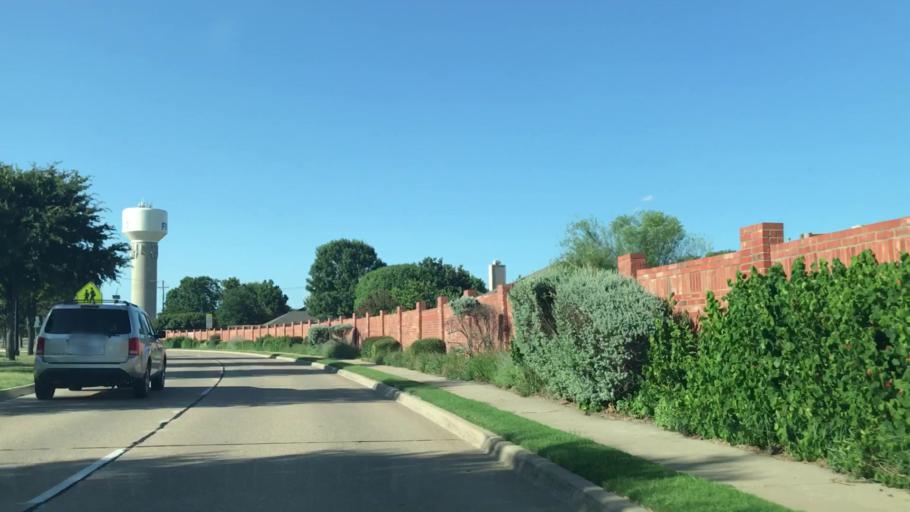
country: US
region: Texas
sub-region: Collin County
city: Frisco
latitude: 33.1292
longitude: -96.7873
